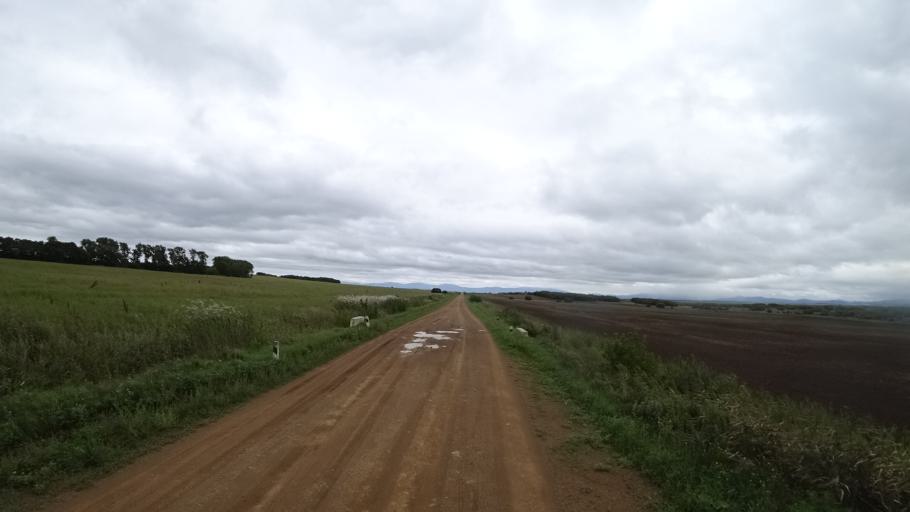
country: RU
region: Primorskiy
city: Chernigovka
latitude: 44.4374
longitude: 132.5798
